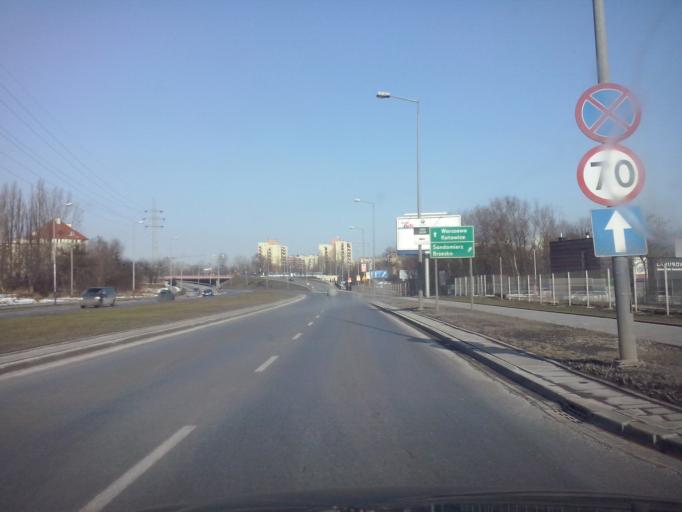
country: PL
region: Lesser Poland Voivodeship
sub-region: Krakow
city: Krakow
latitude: 50.0706
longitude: 20.0050
